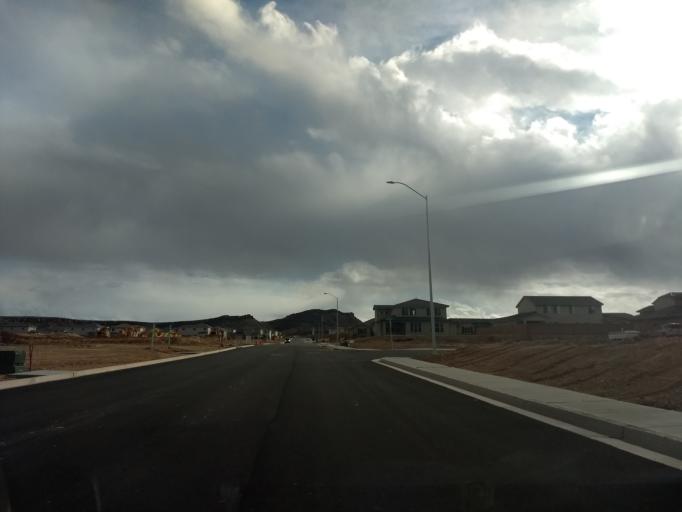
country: US
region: Utah
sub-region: Washington County
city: Washington
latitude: 37.0603
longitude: -113.5176
